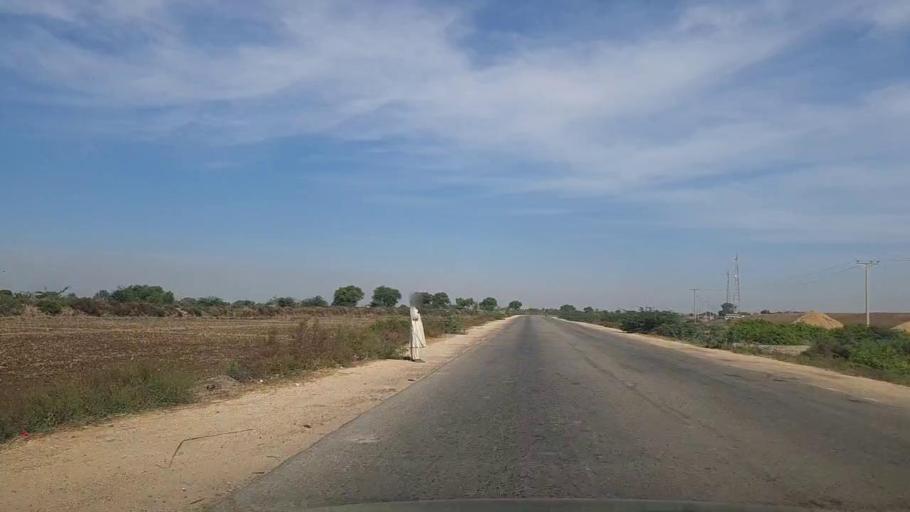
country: PK
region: Sindh
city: Daro Mehar
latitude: 24.9626
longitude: 68.1180
